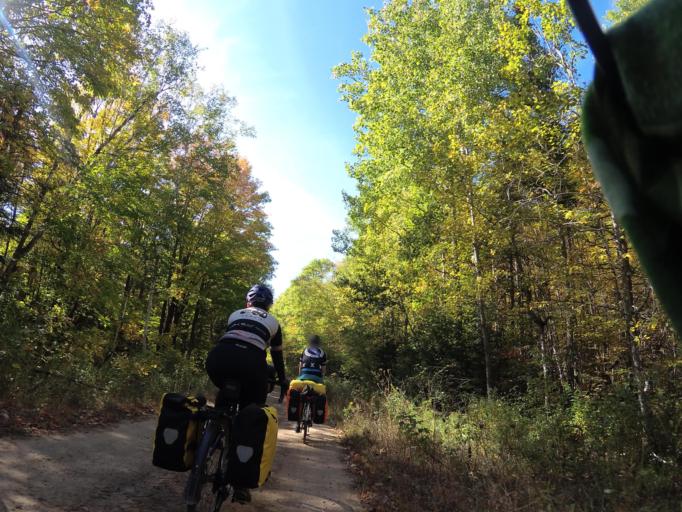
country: CA
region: Ontario
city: Renfrew
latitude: 45.3508
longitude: -77.1231
